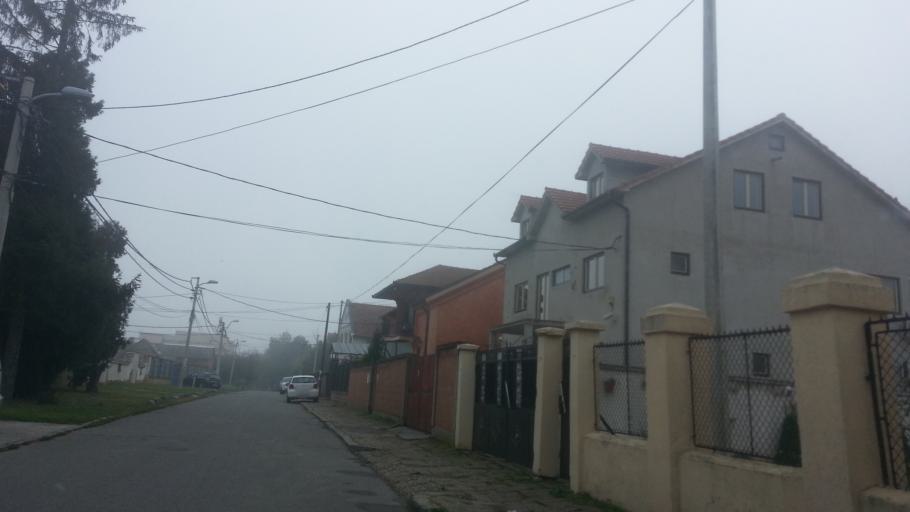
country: RS
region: Central Serbia
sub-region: Belgrade
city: Zemun
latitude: 44.8560
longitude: 20.3883
